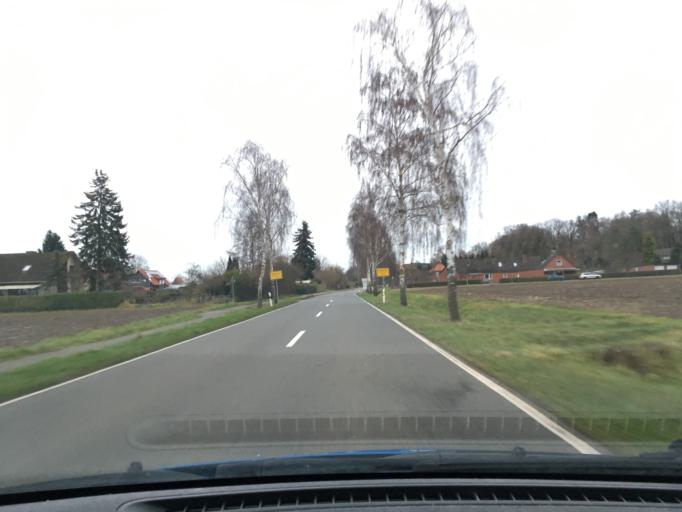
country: DE
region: Lower Saxony
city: Neu Darchau
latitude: 53.2331
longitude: 10.8701
